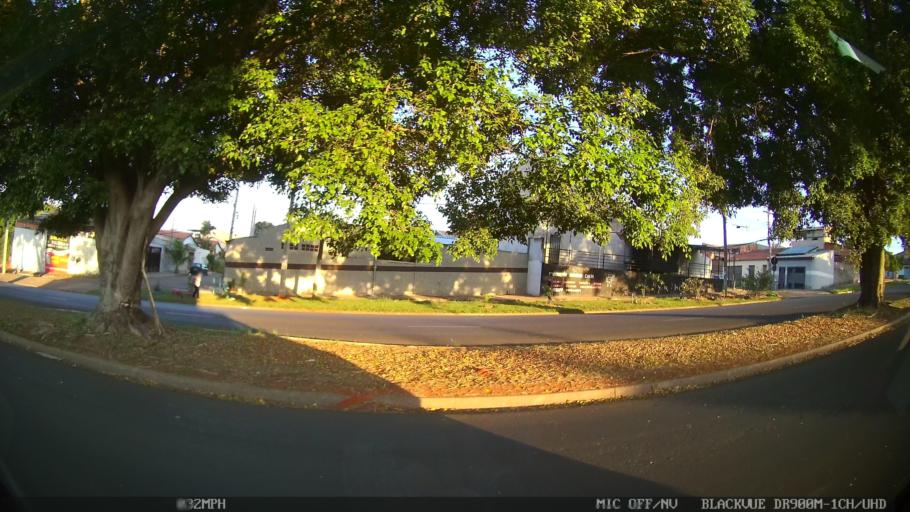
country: BR
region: Sao Paulo
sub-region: Santa Barbara D'Oeste
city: Santa Barbara d'Oeste
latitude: -22.7359
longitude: -47.3940
